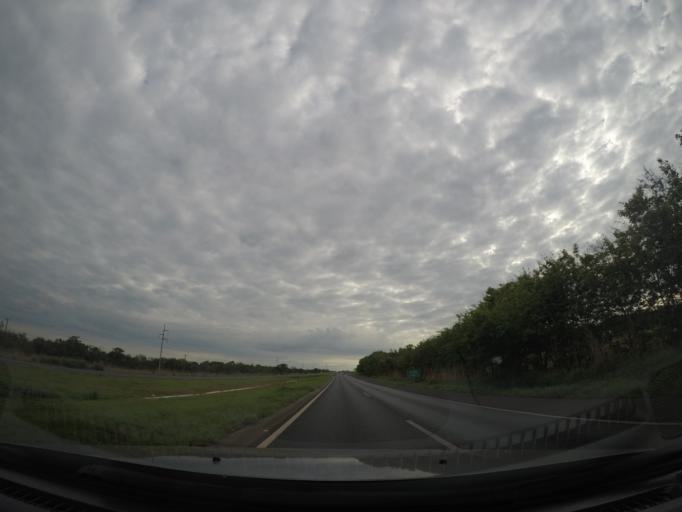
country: BR
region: Goias
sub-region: Planaltina
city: Planaltina
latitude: -15.5980
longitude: -47.6124
